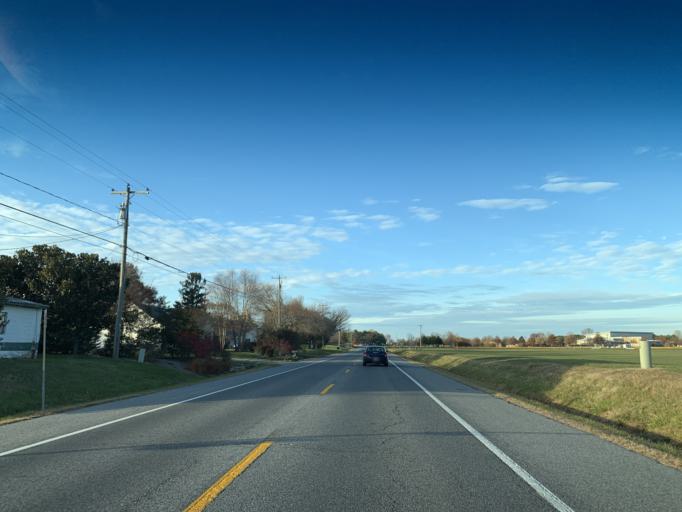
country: US
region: Maryland
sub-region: Kent County
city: Chestertown
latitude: 39.2782
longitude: -76.0933
